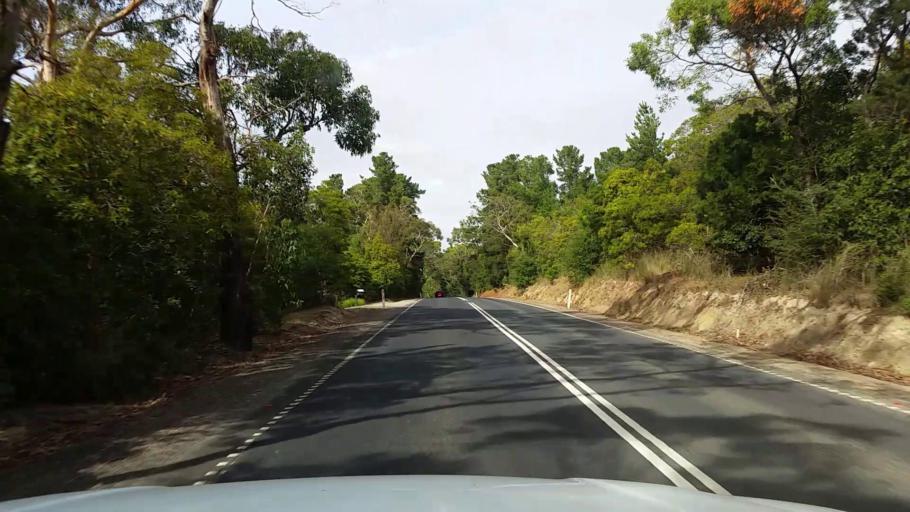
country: AU
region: Victoria
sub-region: Mornington Peninsula
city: Mount Martha
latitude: -38.2907
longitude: 145.0753
